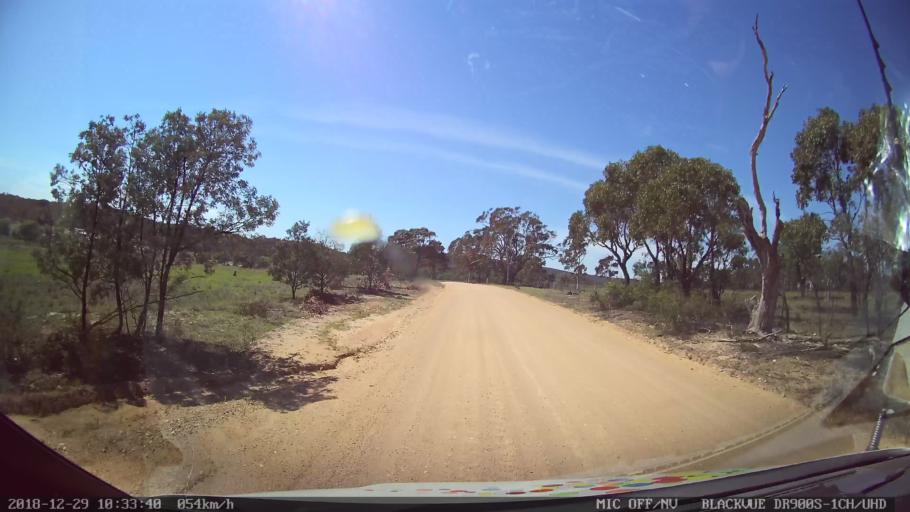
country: AU
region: New South Wales
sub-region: Yass Valley
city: Gundaroo
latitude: -34.9822
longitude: 149.4730
